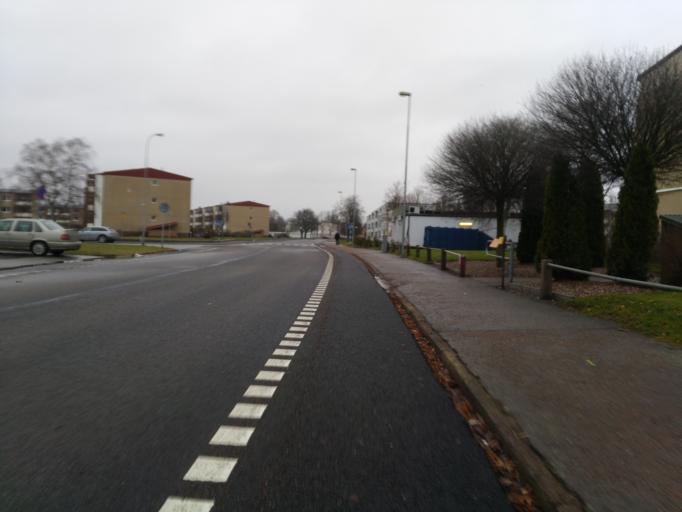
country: SE
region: Vaestra Goetaland
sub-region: Lidkopings Kommun
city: Lidkoping
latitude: 58.4918
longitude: 13.1561
